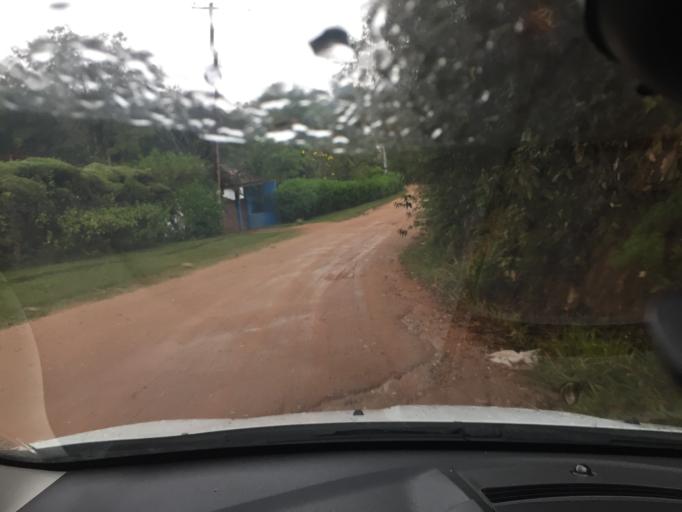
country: BR
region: Sao Paulo
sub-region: Jarinu
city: Jarinu
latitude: -23.1407
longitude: -46.7363
